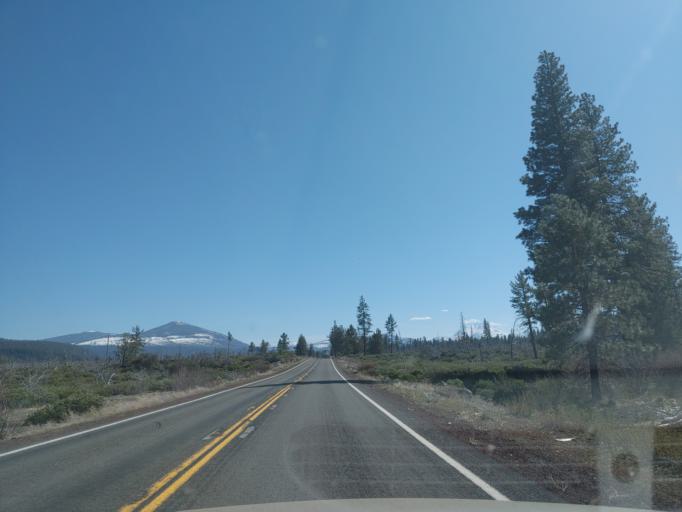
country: US
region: California
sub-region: Shasta County
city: Burney
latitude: 40.7031
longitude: -121.4180
